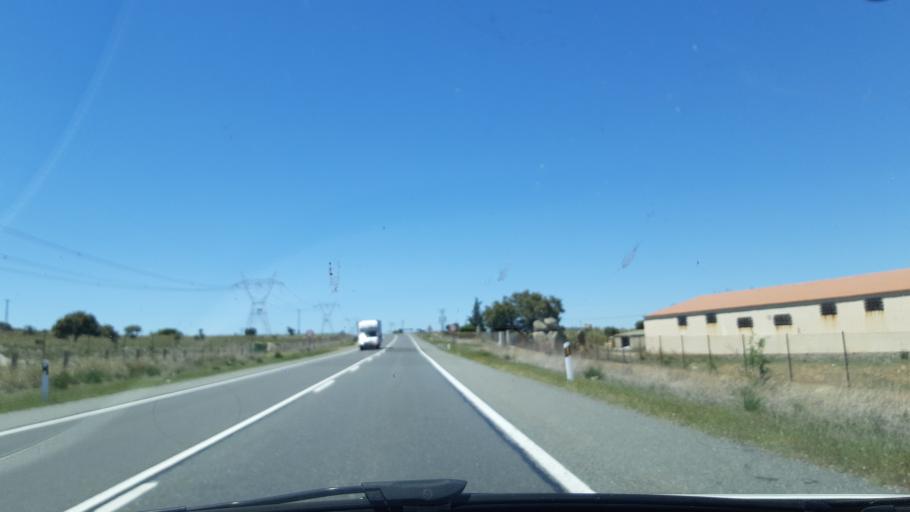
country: ES
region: Castille and Leon
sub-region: Provincia de Segovia
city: Villacastin
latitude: 40.7768
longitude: -4.3913
